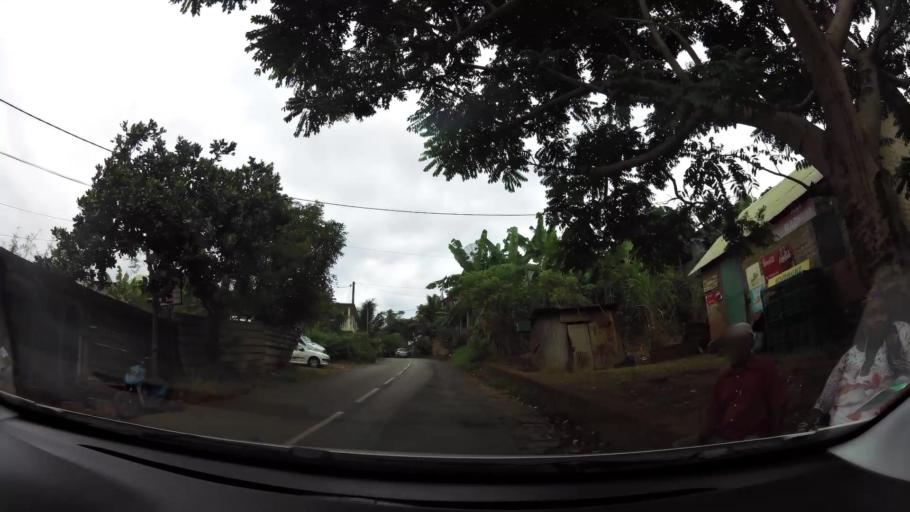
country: YT
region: Chiconi
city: Chiconi
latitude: -12.8375
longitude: 45.1189
